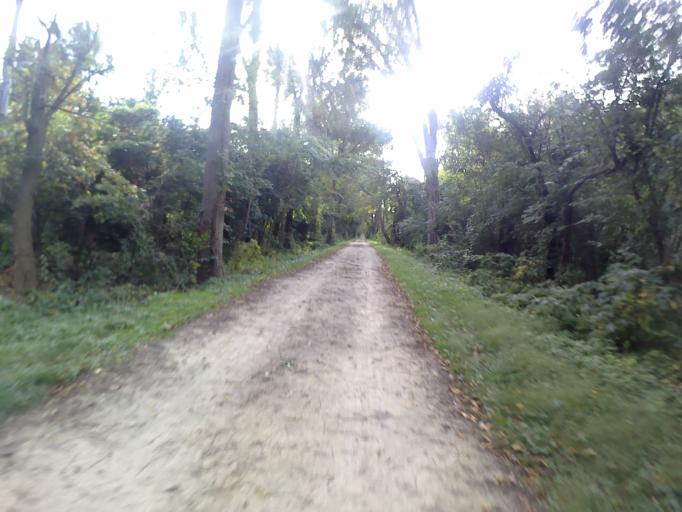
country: US
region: Illinois
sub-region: DuPage County
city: Winfield
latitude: 41.8421
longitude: -88.1350
